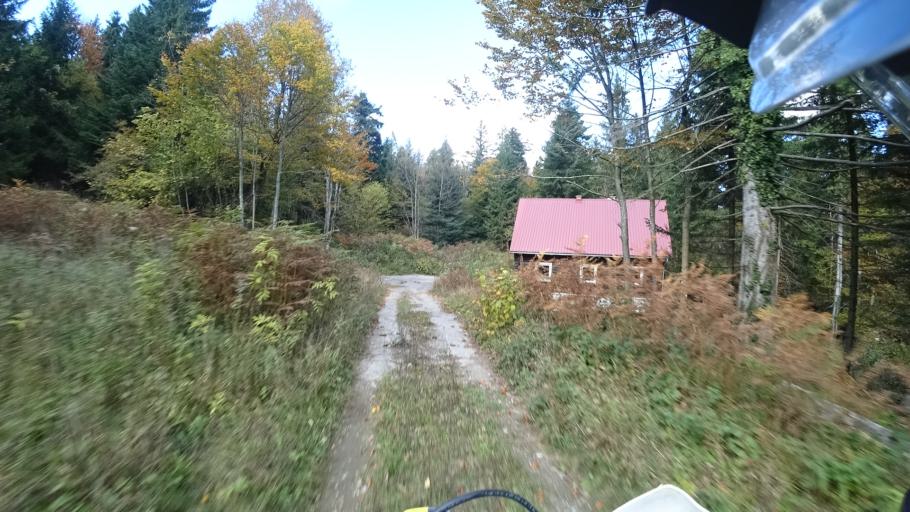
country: HR
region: Karlovacka
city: Plaski
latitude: 45.0701
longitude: 15.3357
